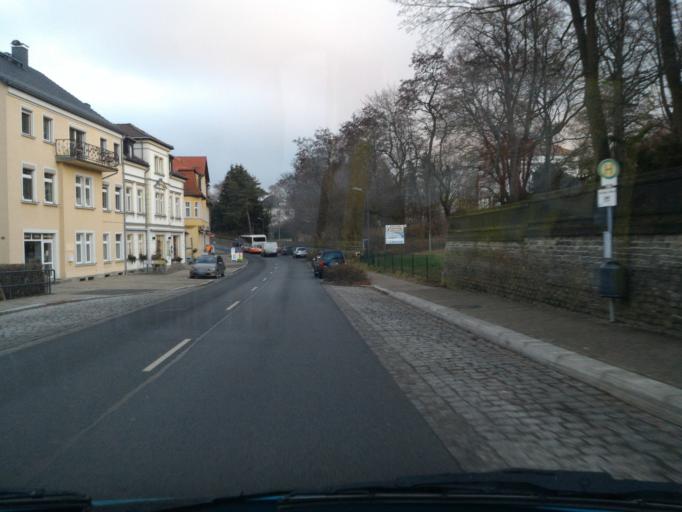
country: DE
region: Saxony
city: Grossschonau
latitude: 50.8977
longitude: 14.6562
